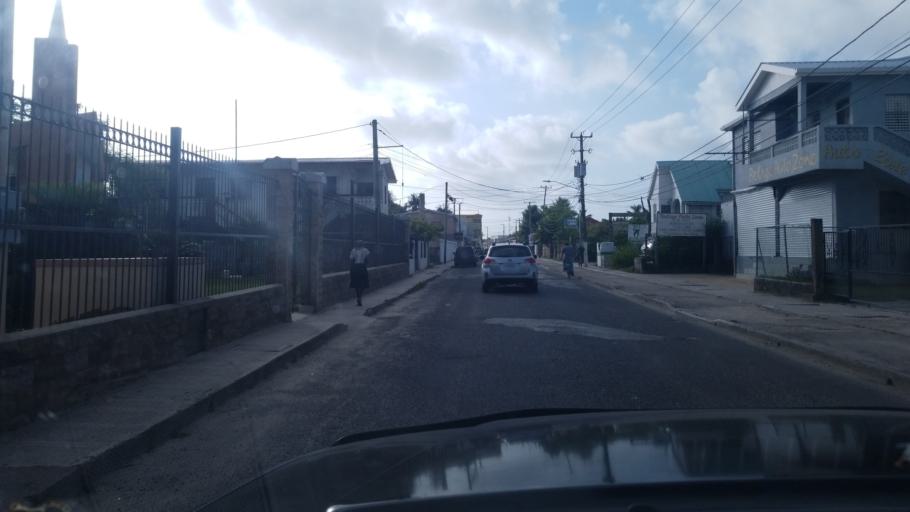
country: BZ
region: Belize
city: Belize City
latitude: 17.4953
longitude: -88.1978
